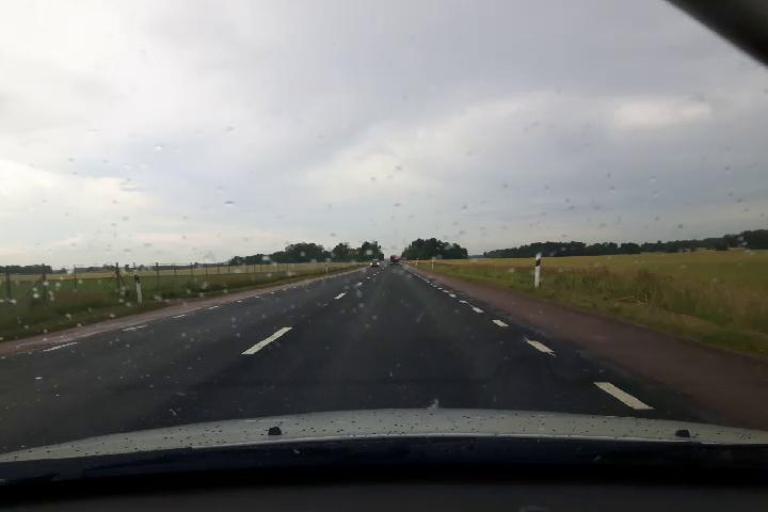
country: SE
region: Uppsala
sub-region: Uppsala Kommun
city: Gamla Uppsala
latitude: 59.9537
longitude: 17.5867
